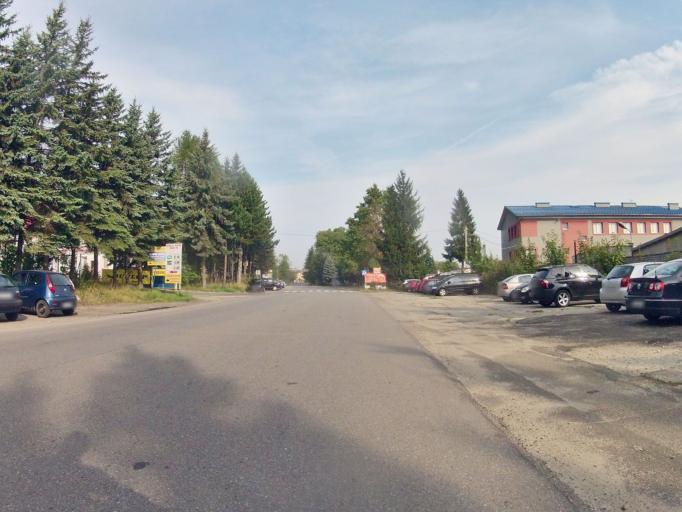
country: PL
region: Subcarpathian Voivodeship
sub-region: Powiat jasielski
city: Jaslo
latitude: 49.7192
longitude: 21.4537
